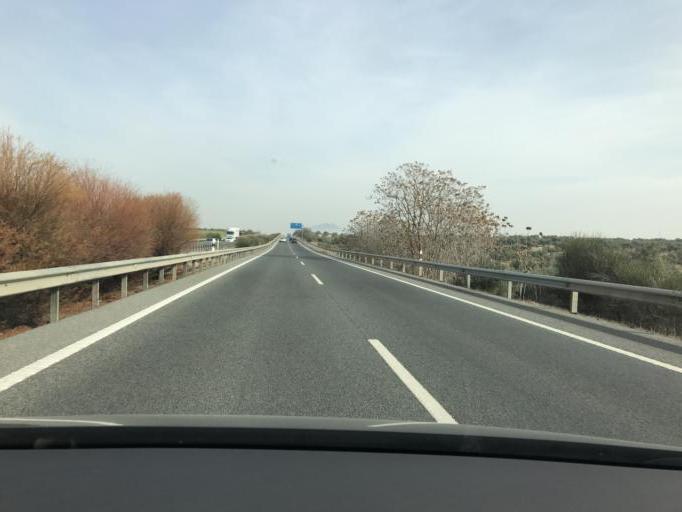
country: ES
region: Andalusia
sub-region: Provincia de Granada
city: Lachar
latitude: 37.1859
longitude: -3.8848
